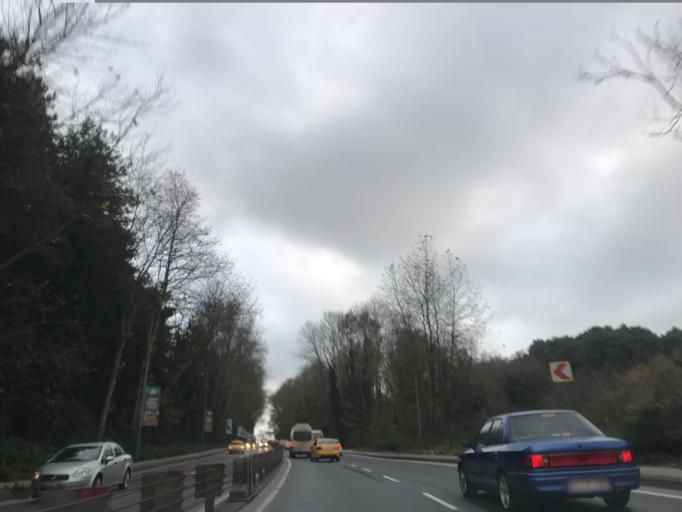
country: TR
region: Istanbul
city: Arikoey
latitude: 41.1473
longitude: 29.0278
